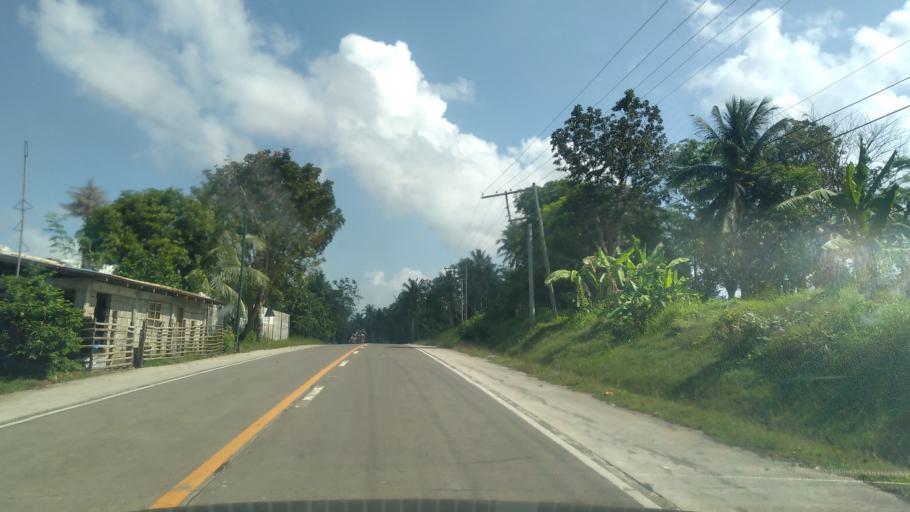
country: PH
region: Calabarzon
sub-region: Province of Quezon
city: Unisan
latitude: 13.8351
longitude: 121.9843
